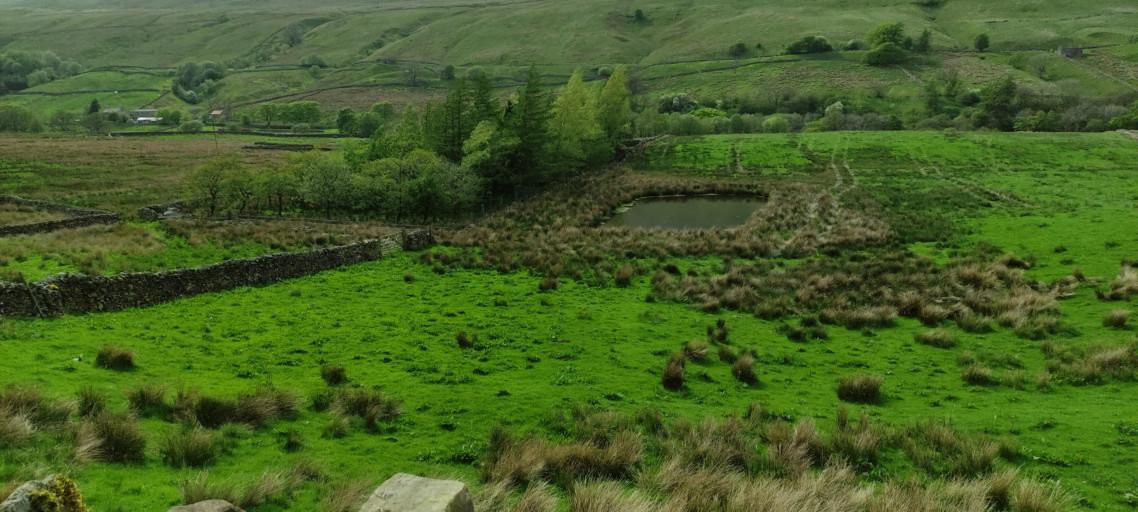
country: GB
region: England
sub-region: Cumbria
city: Kirkby Stephen
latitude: 54.3790
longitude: -2.3383
